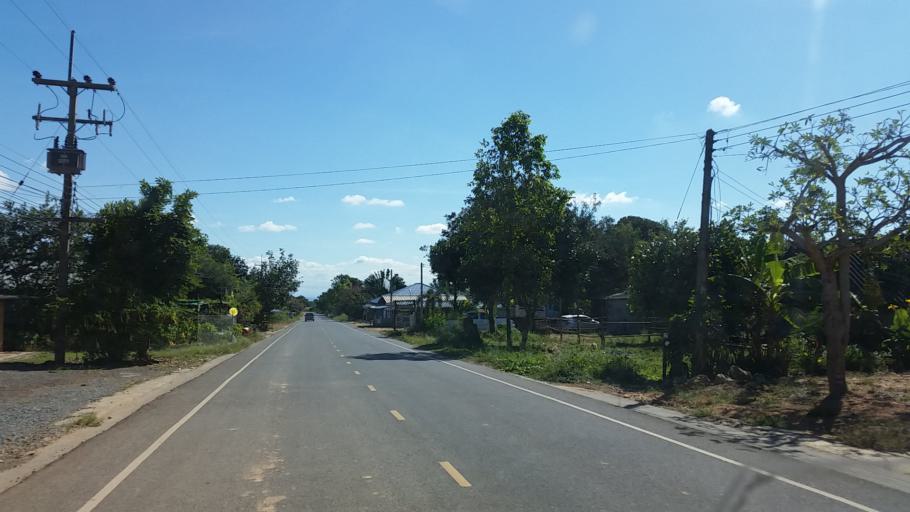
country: TH
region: Chaiyaphum
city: Sap Yai
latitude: 15.6145
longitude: 101.4022
